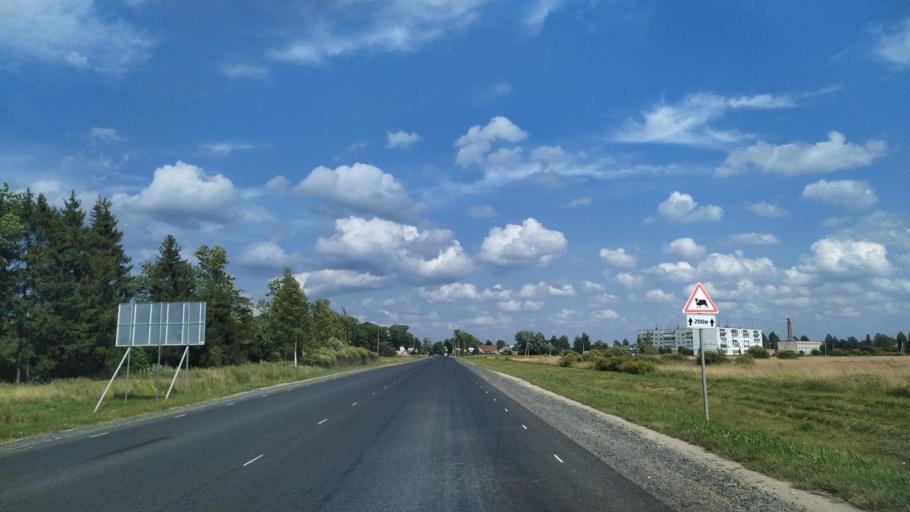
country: RU
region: Pskov
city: Porkhov
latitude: 57.7587
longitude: 29.5377
